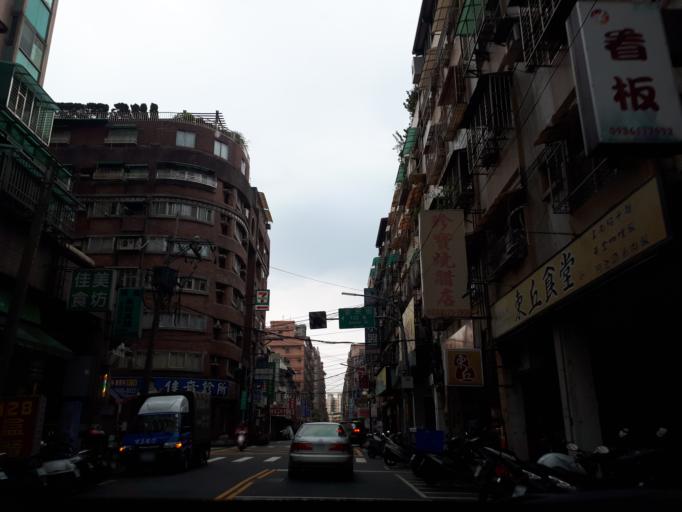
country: TW
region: Taipei
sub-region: Taipei
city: Banqiao
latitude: 24.9689
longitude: 121.5164
